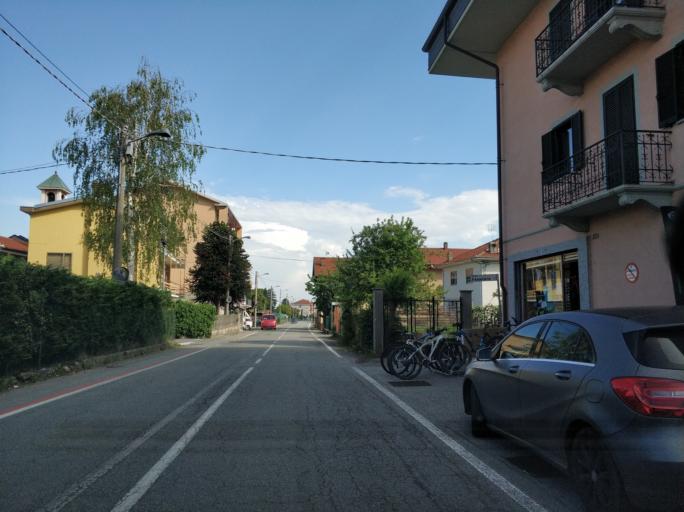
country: IT
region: Piedmont
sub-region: Provincia di Torino
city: Cafasse
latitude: 45.2535
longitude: 7.5108
